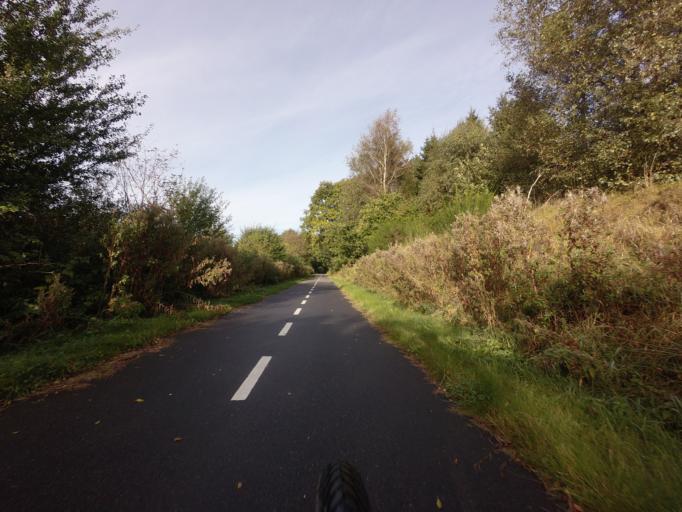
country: DK
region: Central Jutland
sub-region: Viborg Kommune
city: Viborg
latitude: 56.4271
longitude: 9.4196
